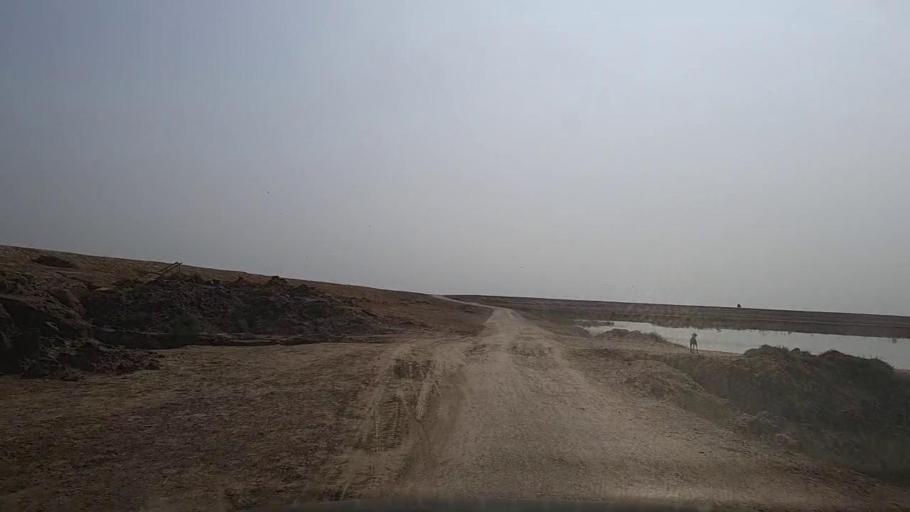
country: PK
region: Sindh
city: Thatta
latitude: 24.5741
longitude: 67.9161
